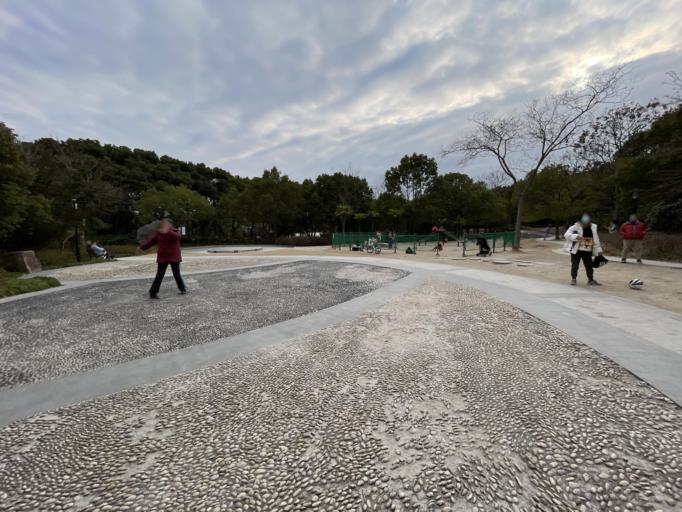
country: CN
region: Shanghai Shi
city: Yangpu
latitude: 31.2952
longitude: 121.5239
